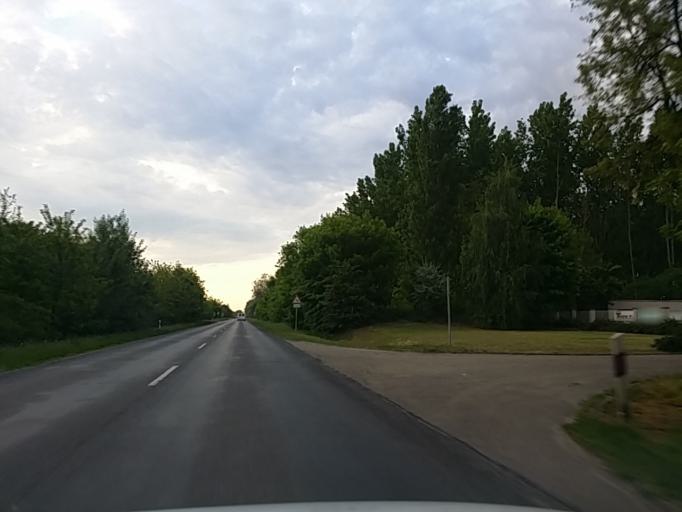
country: HU
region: Bacs-Kiskun
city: Lajosmizse
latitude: 47.0055
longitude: 19.5882
